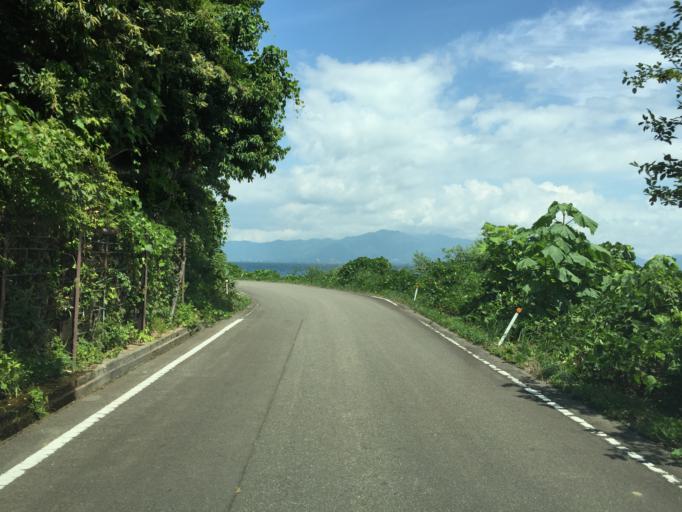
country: JP
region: Fukushima
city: Inawashiro
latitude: 37.4887
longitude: 140.0312
